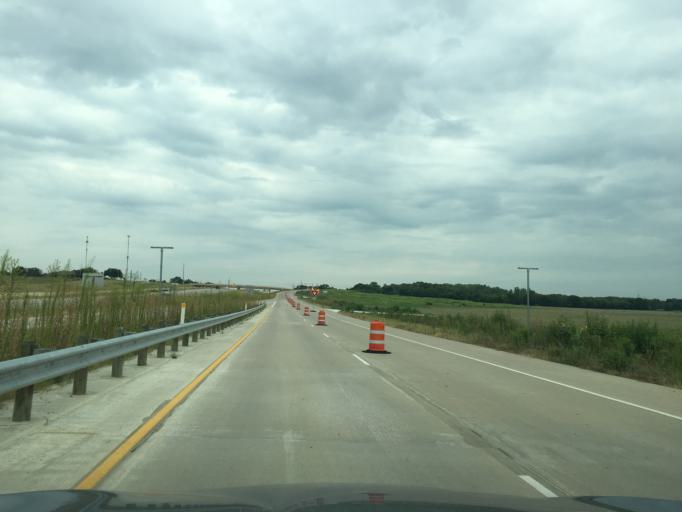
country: US
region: Texas
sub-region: Collin County
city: Melissa
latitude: 33.3033
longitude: -96.5907
